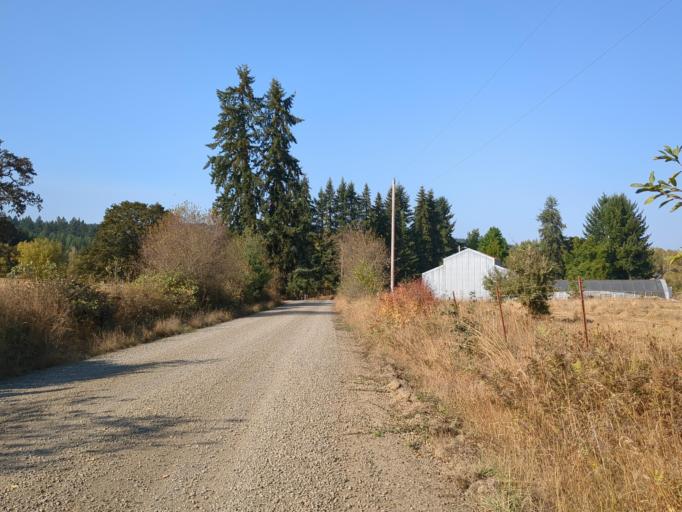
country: US
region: Oregon
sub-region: Lane County
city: Junction City
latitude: 44.2958
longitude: -123.3639
